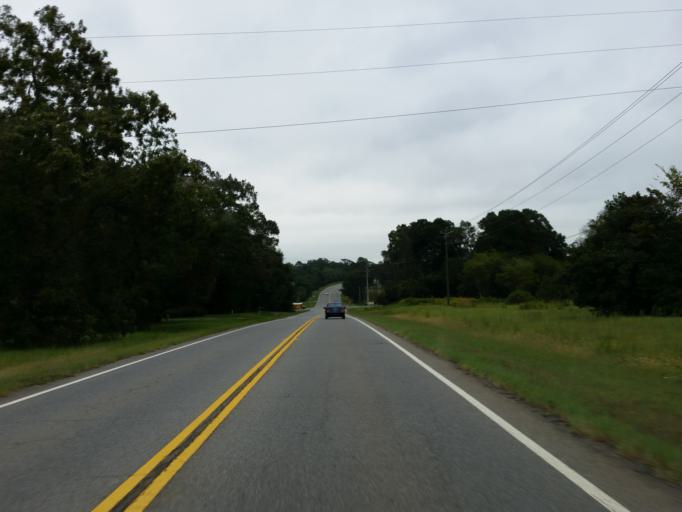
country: US
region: Georgia
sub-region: Houston County
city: Perry
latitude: 32.4815
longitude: -83.7626
